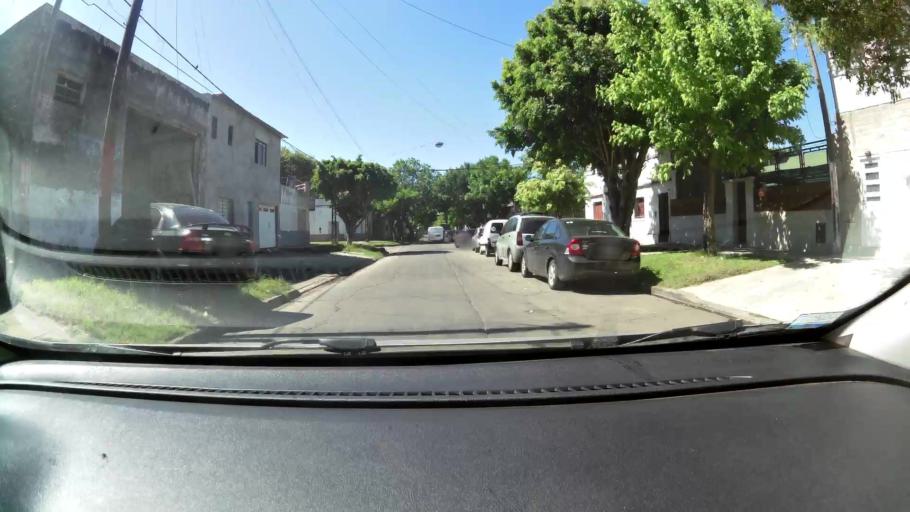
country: AR
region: Santa Fe
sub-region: Departamento de Rosario
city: Rosario
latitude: -32.9455
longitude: -60.6879
